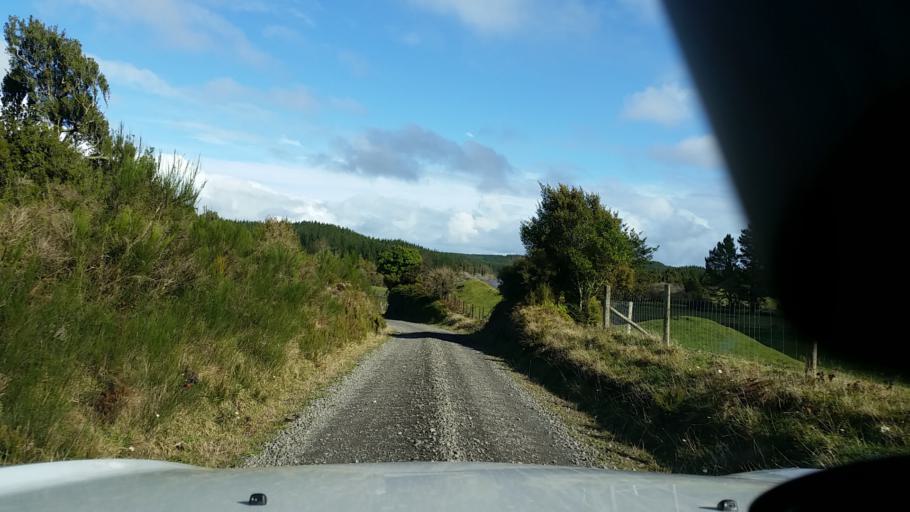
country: NZ
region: Bay of Plenty
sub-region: Rotorua District
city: Rotorua
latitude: -37.9885
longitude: 176.1637
